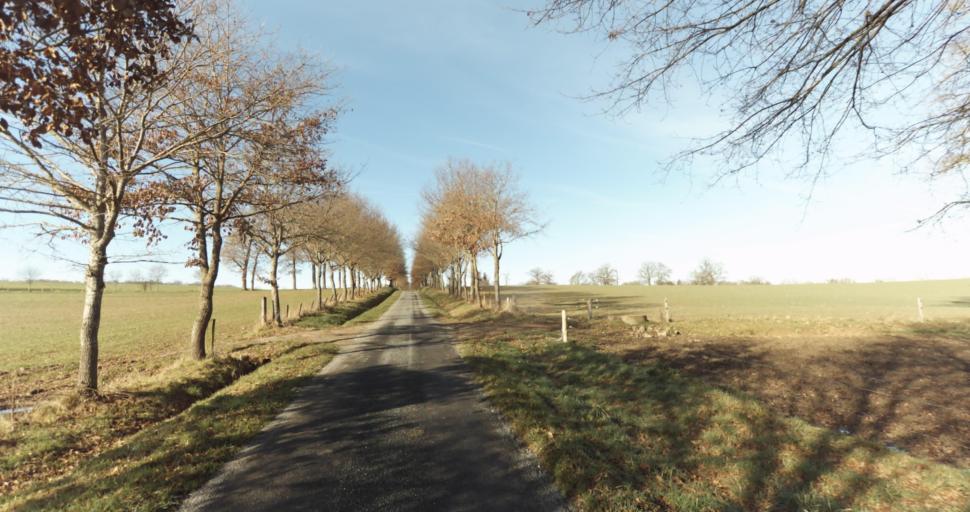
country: FR
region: Limousin
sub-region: Departement de la Haute-Vienne
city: Saint-Priest-sous-Aixe
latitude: 45.7852
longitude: 1.1087
